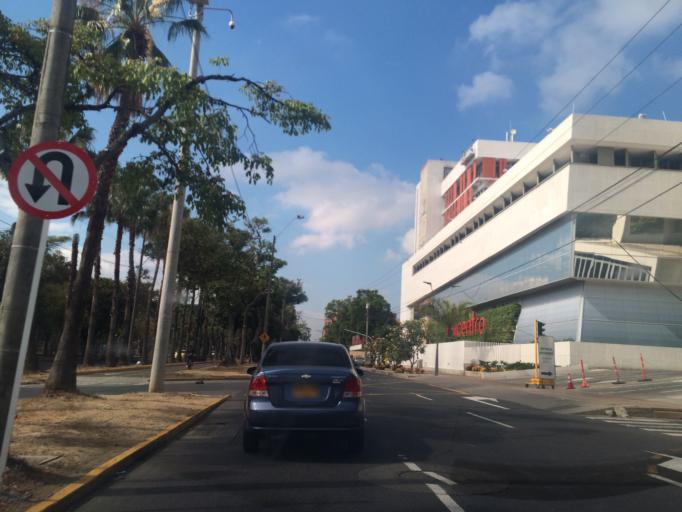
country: CO
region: Valle del Cauca
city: Cali
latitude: 3.3761
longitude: -76.5374
